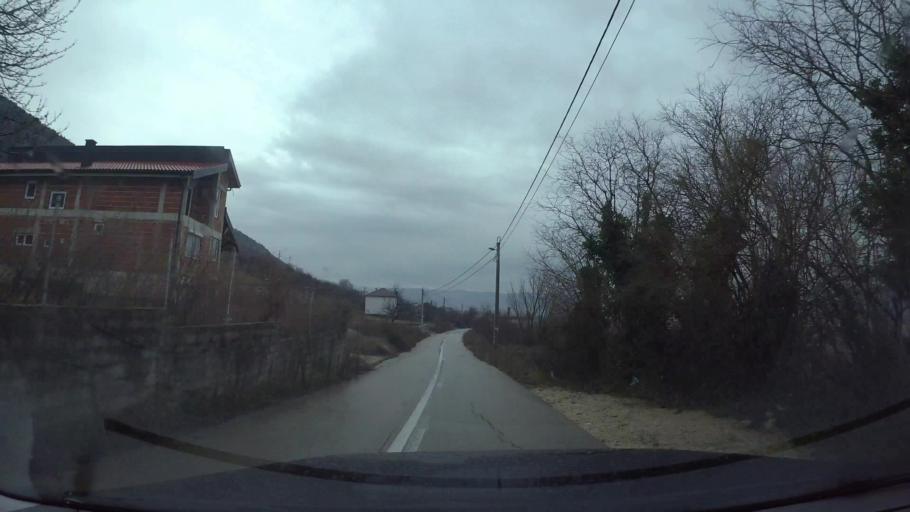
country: BA
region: Federation of Bosnia and Herzegovina
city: Blagaj
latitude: 43.2980
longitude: 17.8555
